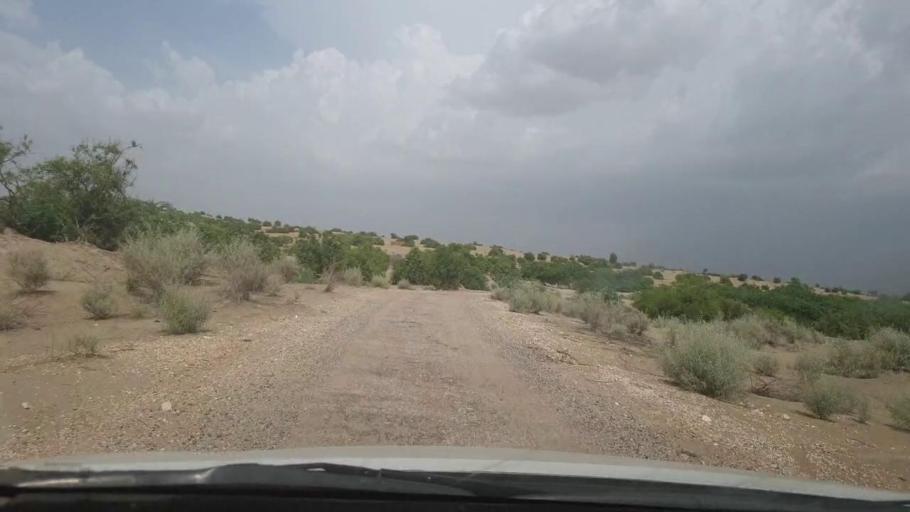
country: PK
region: Sindh
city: Kot Diji
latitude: 27.3375
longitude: 69.0425
